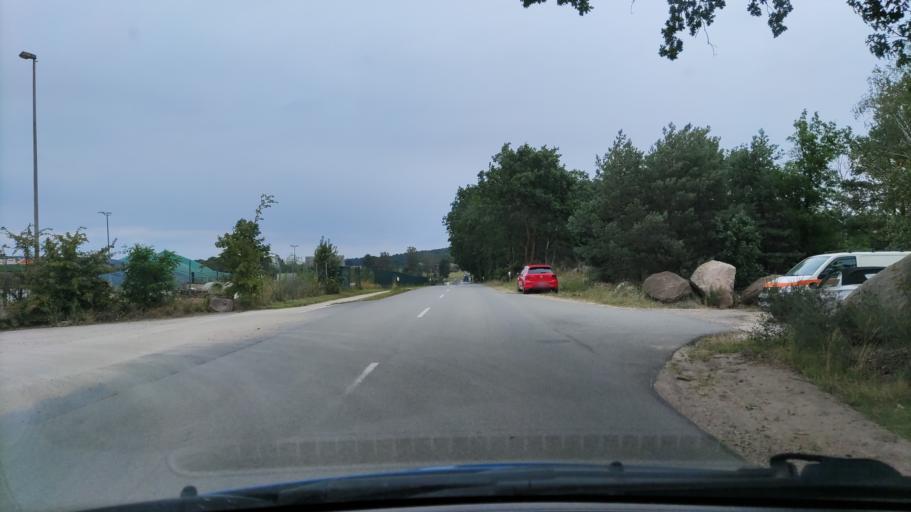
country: DE
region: Lower Saxony
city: Rosche
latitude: 52.9936
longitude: 10.7656
